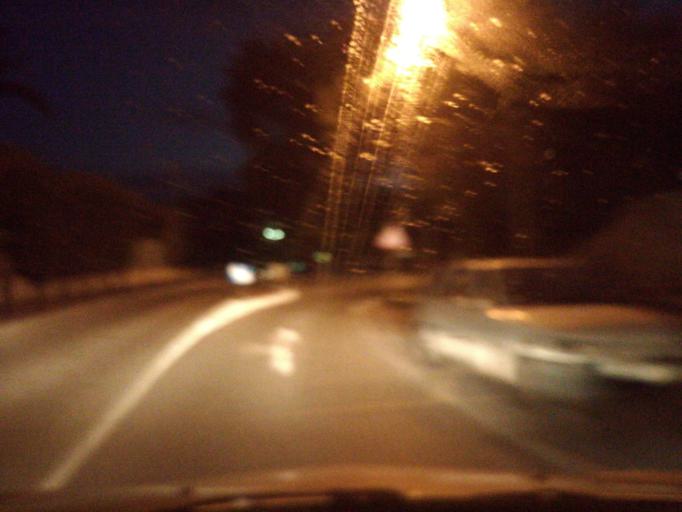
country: FR
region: Provence-Alpes-Cote d'Azur
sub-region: Departement des Alpes-Maritimes
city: Grasse
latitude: 43.6388
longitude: 6.9111
